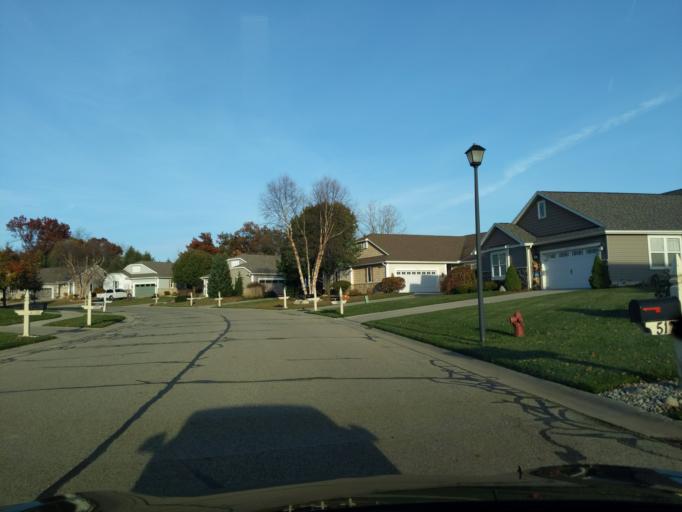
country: US
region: Michigan
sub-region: Clinton County
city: Bath
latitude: 42.7950
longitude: -84.4596
